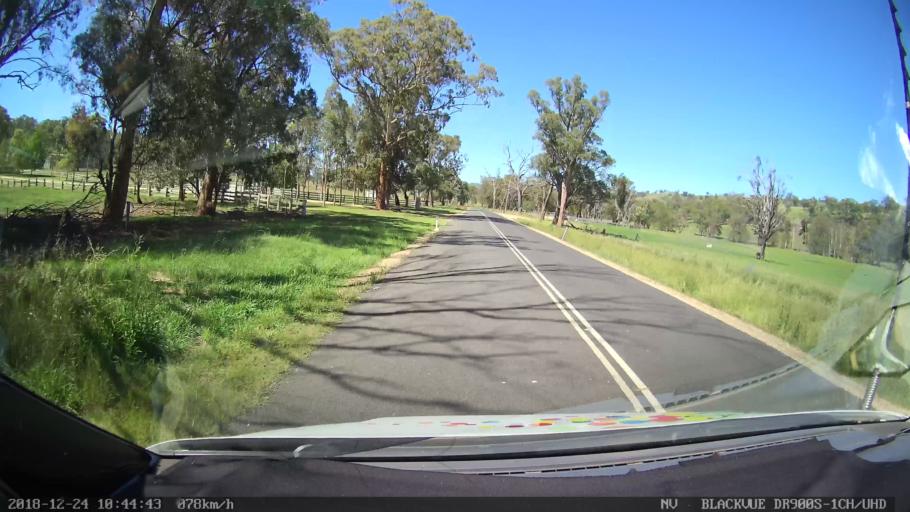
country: AU
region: New South Wales
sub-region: Upper Hunter Shire
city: Merriwa
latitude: -31.8958
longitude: 150.4417
